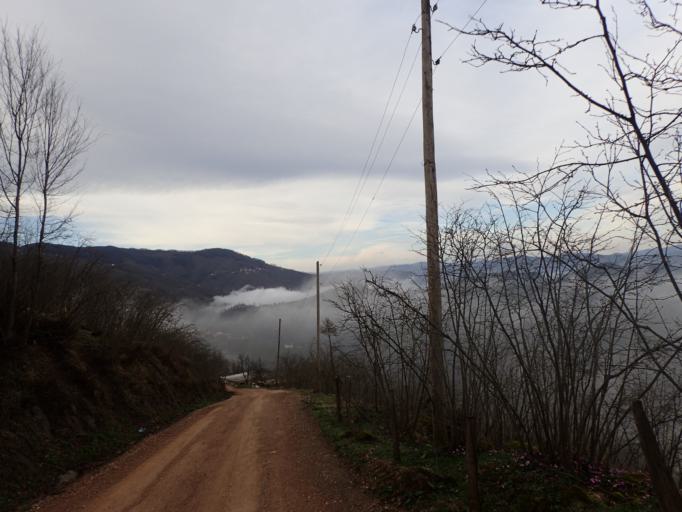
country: TR
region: Ordu
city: Camas
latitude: 40.8875
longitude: 37.5301
